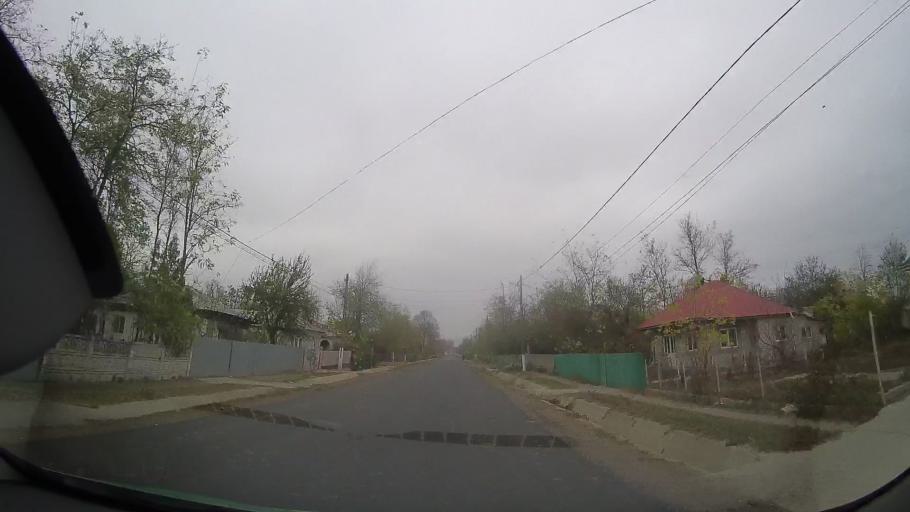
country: RO
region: Braila
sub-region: Comuna Rosiori
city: Rosiori
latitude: 44.8109
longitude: 27.3877
